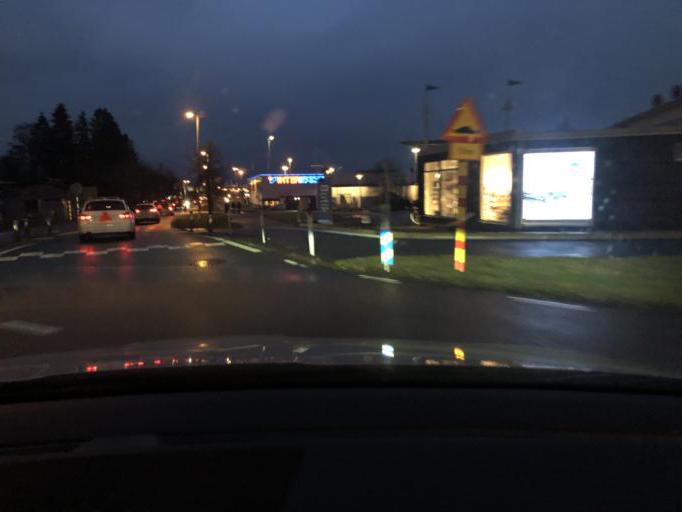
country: SE
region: Joenkoeping
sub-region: Jonkopings Kommun
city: Jonkoping
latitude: 57.7675
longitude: 14.2009
